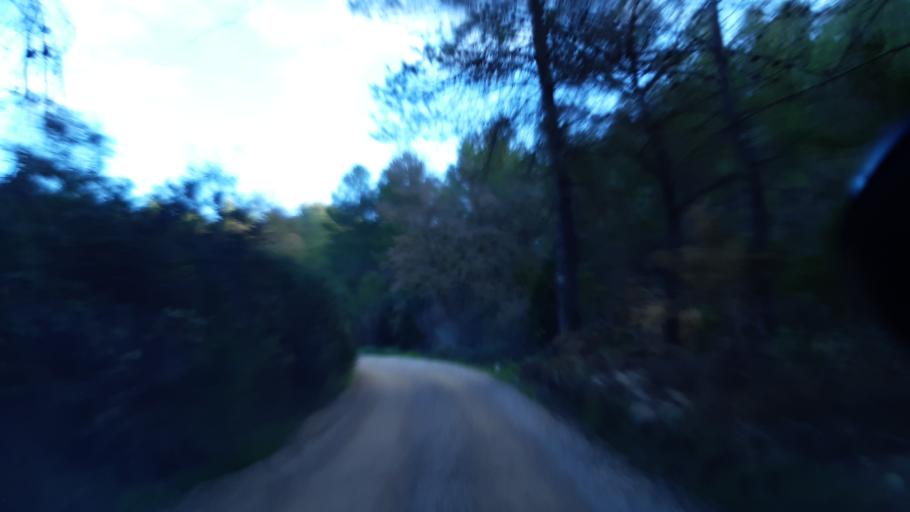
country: ES
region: Aragon
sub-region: Provincia de Teruel
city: Valderrobres
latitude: 40.8492
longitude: 0.2155
